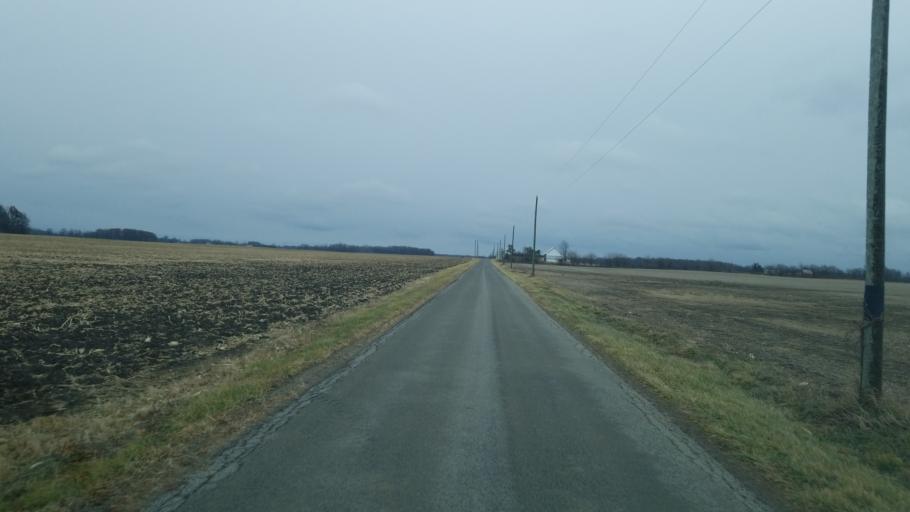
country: US
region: Ohio
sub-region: Union County
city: Marysville
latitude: 40.3110
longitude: -83.3241
